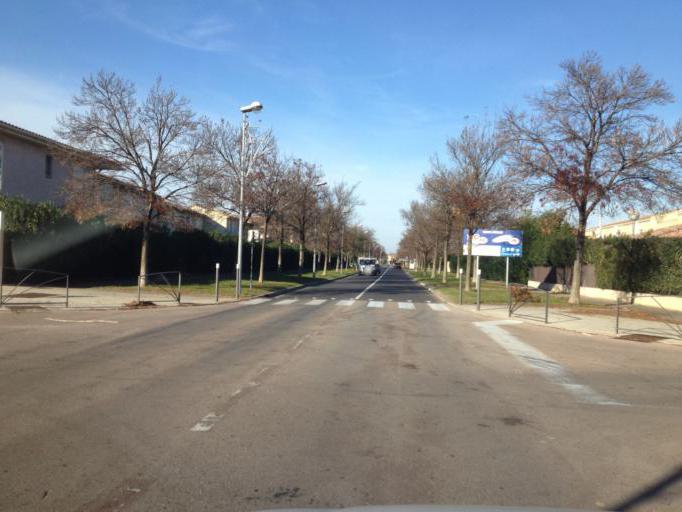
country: FR
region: Provence-Alpes-Cote d'Azur
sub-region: Departement des Bouches-du-Rhone
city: Istres
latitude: 43.5017
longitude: 4.9704
